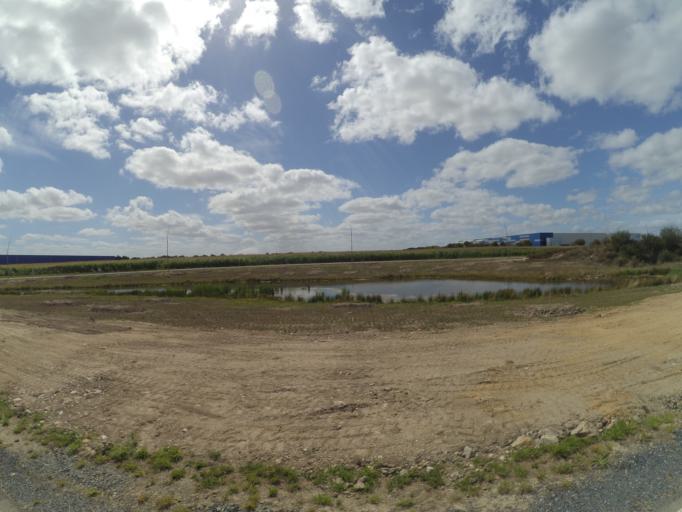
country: FR
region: Pays de la Loire
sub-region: Departement de la Vendee
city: Saint-Hilaire-de-Loulay
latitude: 47.0239
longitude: -1.3517
